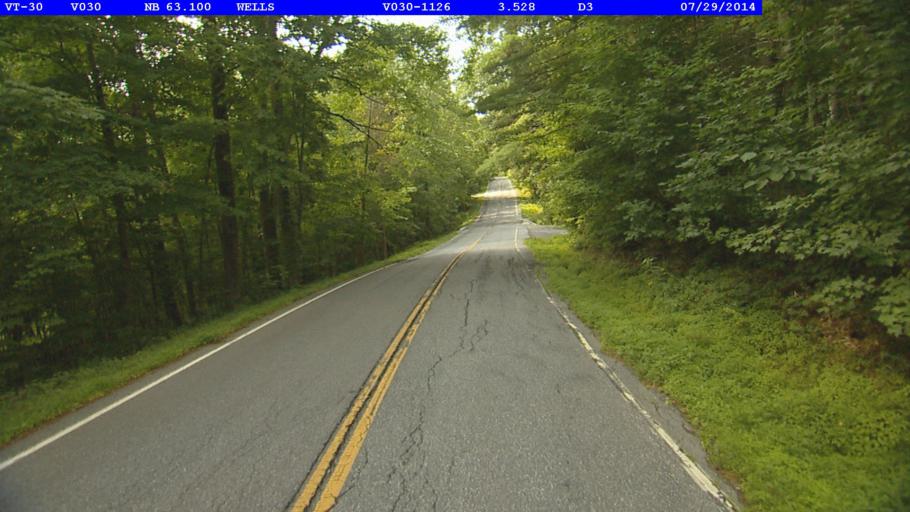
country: US
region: New York
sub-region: Washington County
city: Granville
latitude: 43.4432
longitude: -73.1988
